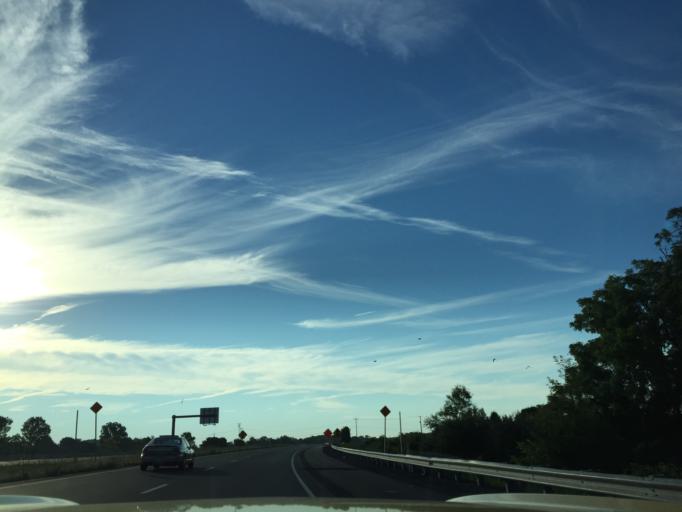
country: US
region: Pennsylvania
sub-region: Lehigh County
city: Ancient Oaks
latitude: 40.5650
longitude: -75.5909
